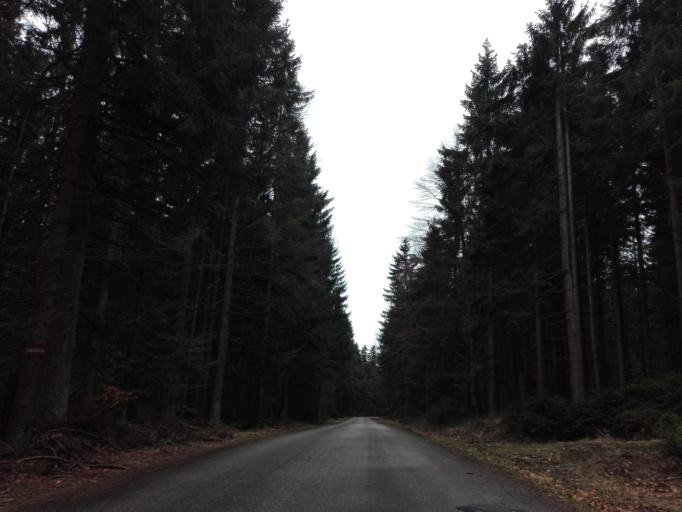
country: AT
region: Upper Austria
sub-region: Politischer Bezirk Rohrbach
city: Aigen im Muehlkreis
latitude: 48.6989
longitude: 13.9706
